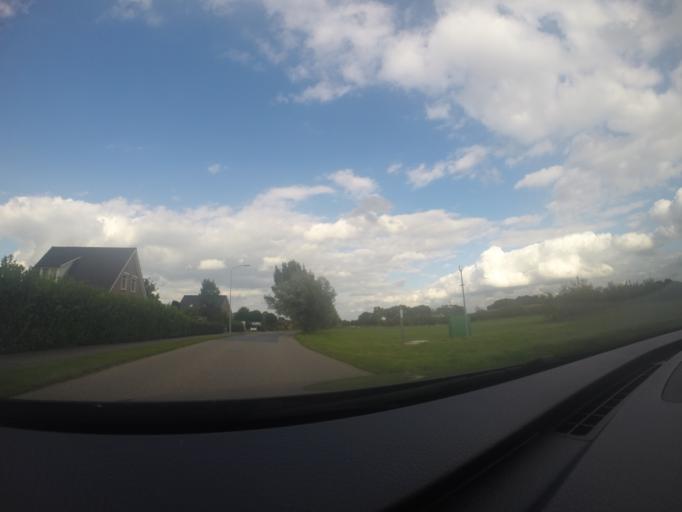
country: NL
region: Gelderland
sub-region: Gemeente Doesburg
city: Doesburg
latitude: 52.0239
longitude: 6.1848
